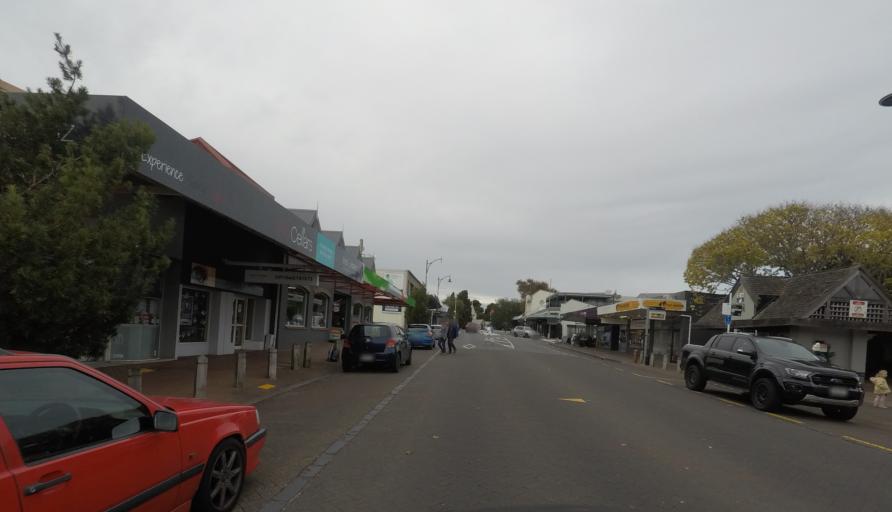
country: NZ
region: Auckland
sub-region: Auckland
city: Pakuranga
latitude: -36.8946
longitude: 174.9324
